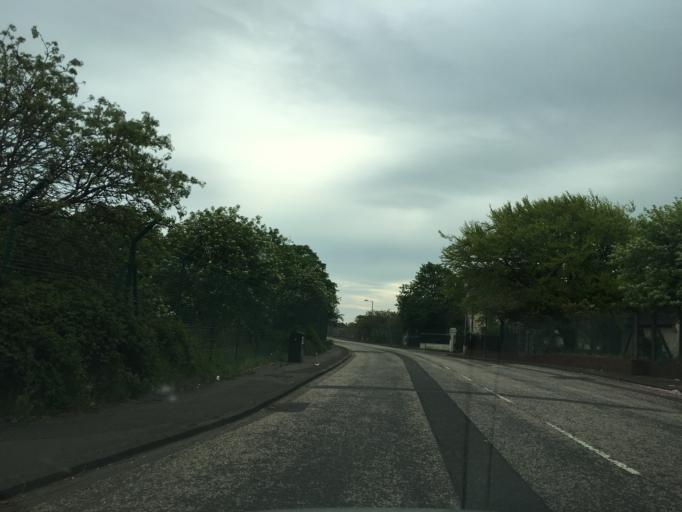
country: GB
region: Scotland
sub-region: Edinburgh
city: Ratho
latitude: 55.9518
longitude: -3.3473
